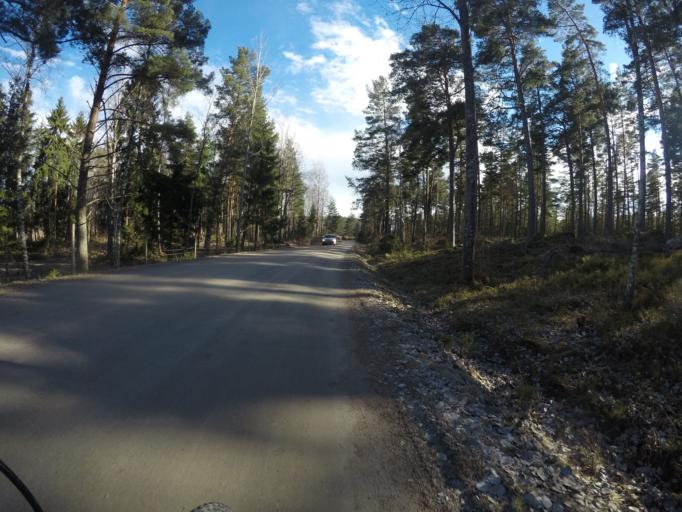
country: SE
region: Soedermanland
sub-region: Eskilstuna Kommun
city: Kvicksund
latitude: 59.4180
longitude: 16.2382
